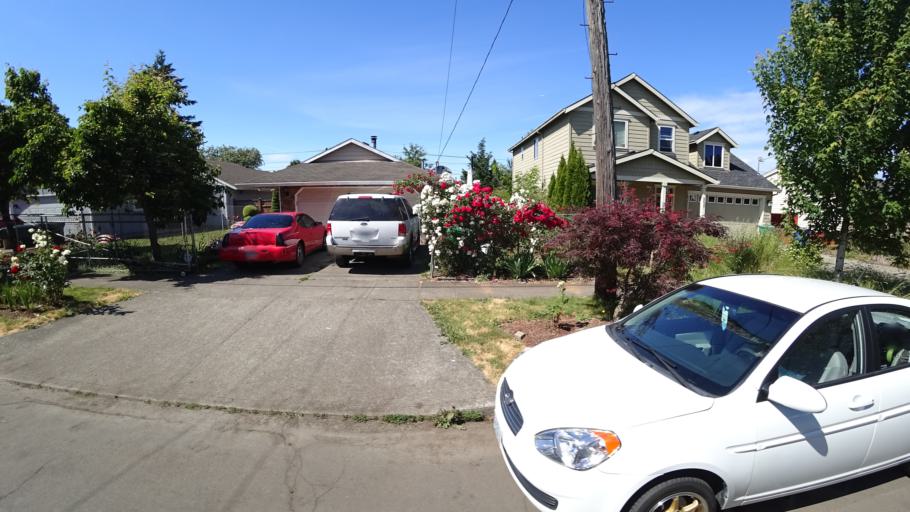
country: US
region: Washington
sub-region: Clark County
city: Vancouver
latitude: 45.5945
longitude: -122.7313
